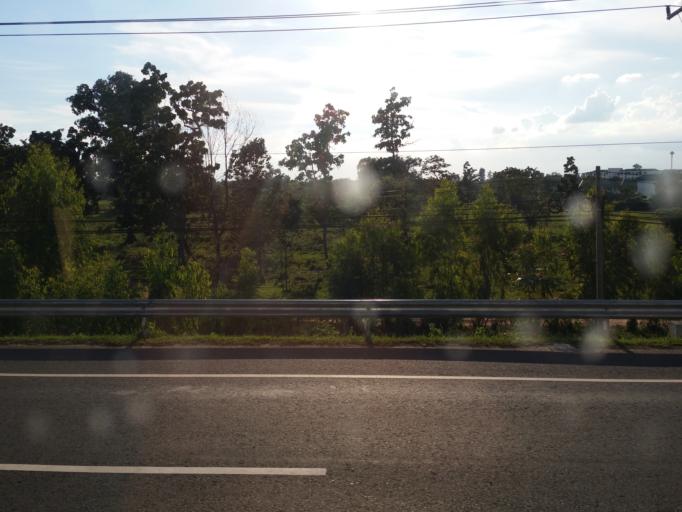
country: TH
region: Changwat Ubon Ratchathani
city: Sirindhorn
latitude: 15.1904
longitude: 105.3675
